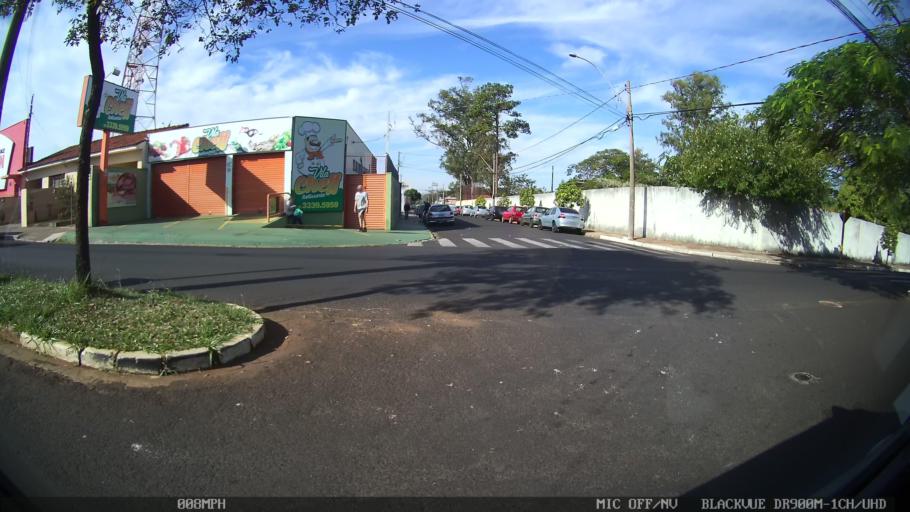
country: BR
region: Sao Paulo
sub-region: Araraquara
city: Araraquara
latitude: -21.7877
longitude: -48.1576
